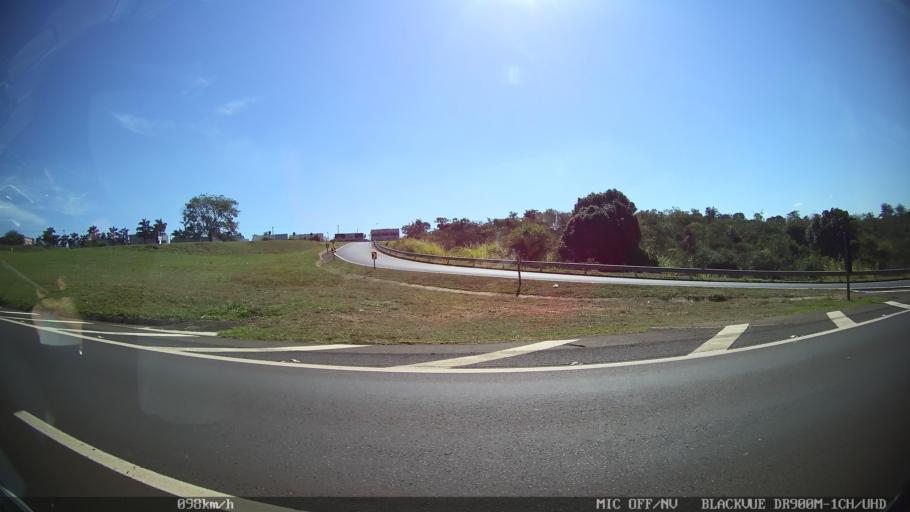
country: BR
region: Sao Paulo
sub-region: Franca
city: Franca
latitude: -20.5571
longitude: -47.4384
